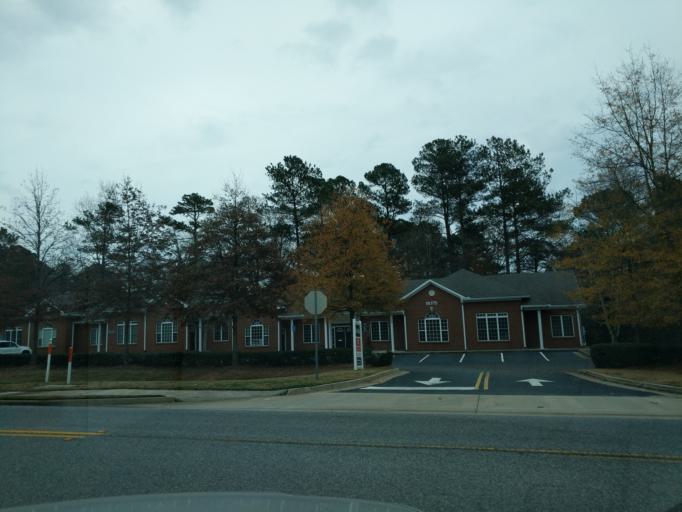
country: US
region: Georgia
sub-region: Fulton County
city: Alpharetta
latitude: 34.0326
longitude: -84.2902
